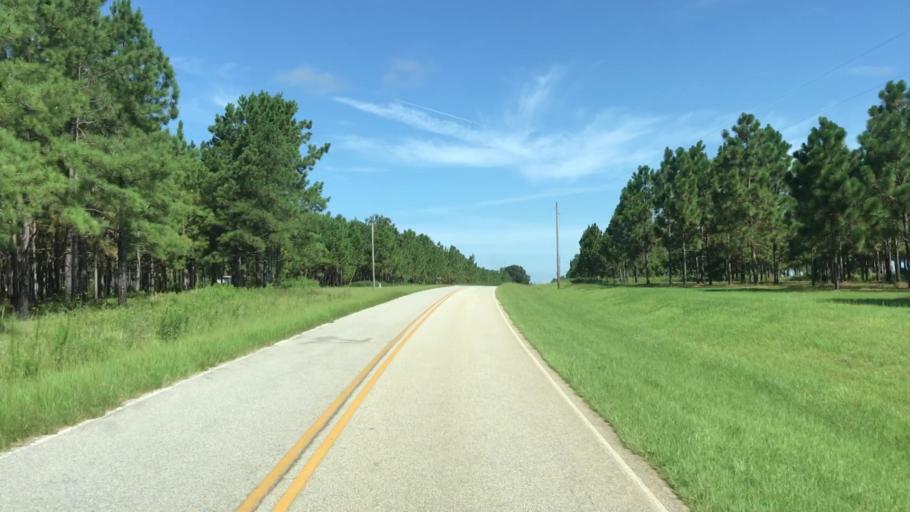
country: US
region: Georgia
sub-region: Jefferson County
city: Wadley
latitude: 32.8268
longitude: -82.3830
